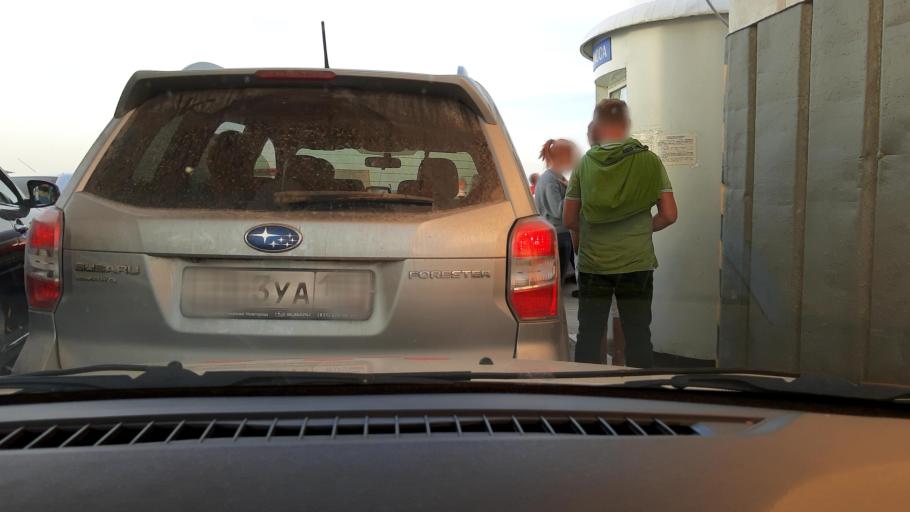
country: RU
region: Nizjnij Novgorod
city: Nizhniy Novgorod
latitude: 56.3345
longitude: 44.0252
